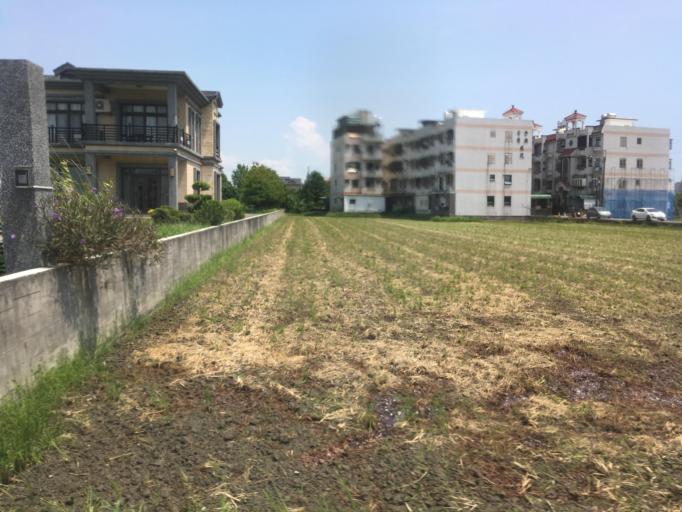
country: TW
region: Taiwan
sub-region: Yilan
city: Yilan
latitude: 24.6746
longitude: 121.8057
